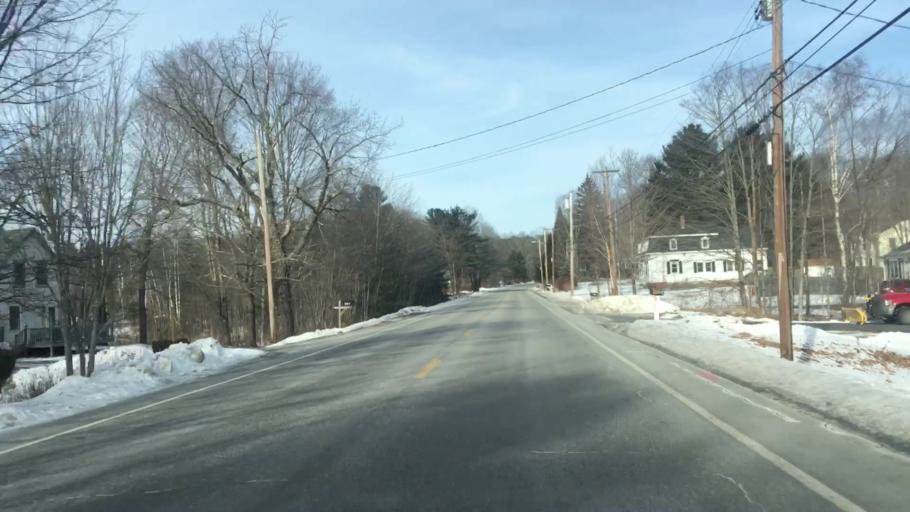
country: US
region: Maine
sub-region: Cumberland County
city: South Windham
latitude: 43.7546
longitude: -70.4249
